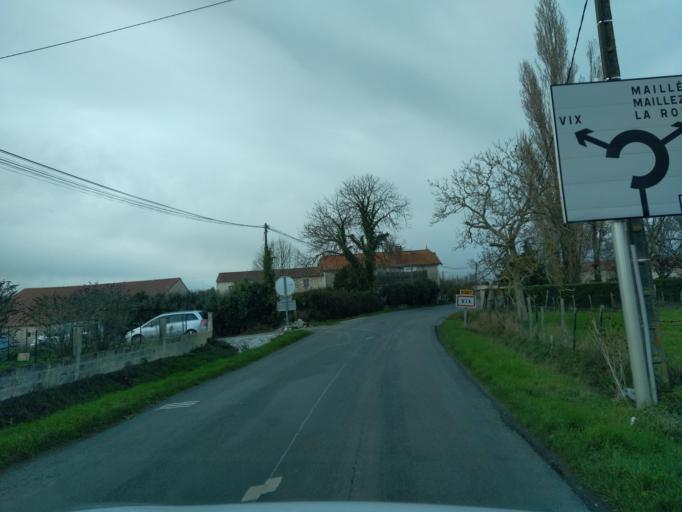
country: FR
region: Pays de la Loire
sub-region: Departement de la Vendee
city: Vix
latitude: 46.3522
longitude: -0.8404
